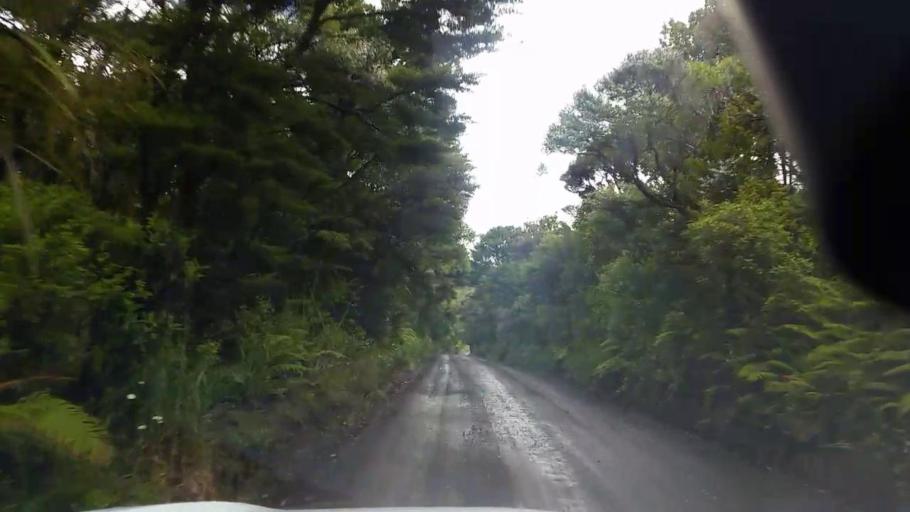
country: NZ
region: Auckland
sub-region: Auckland
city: Muriwai Beach
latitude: -36.9294
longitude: 174.5029
